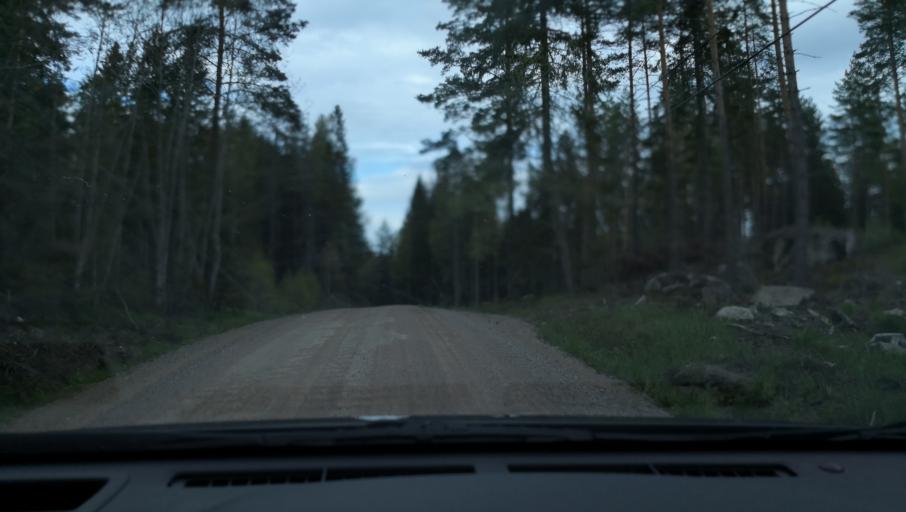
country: SE
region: Vaestmanland
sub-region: Fagersta Kommun
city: Fagersta
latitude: 60.1095
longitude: 15.7978
